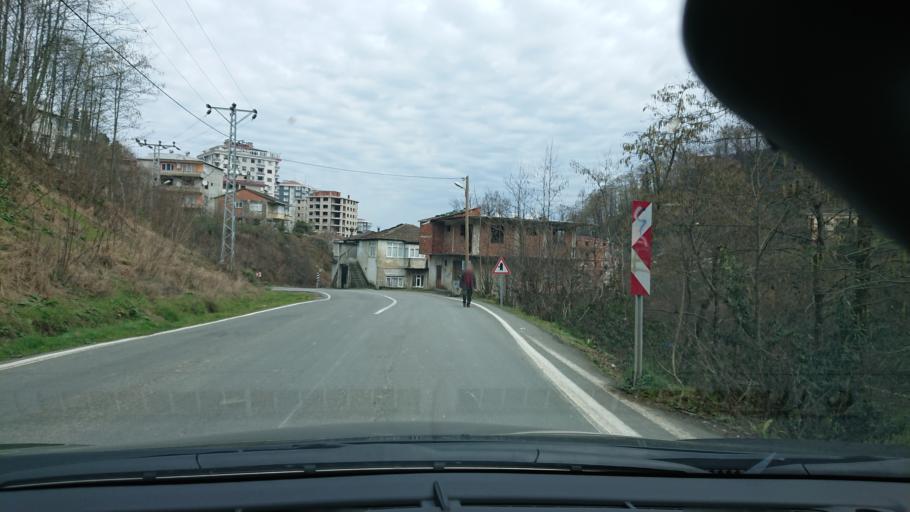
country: TR
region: Rize
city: Rize
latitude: 41.0274
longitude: 40.5062
